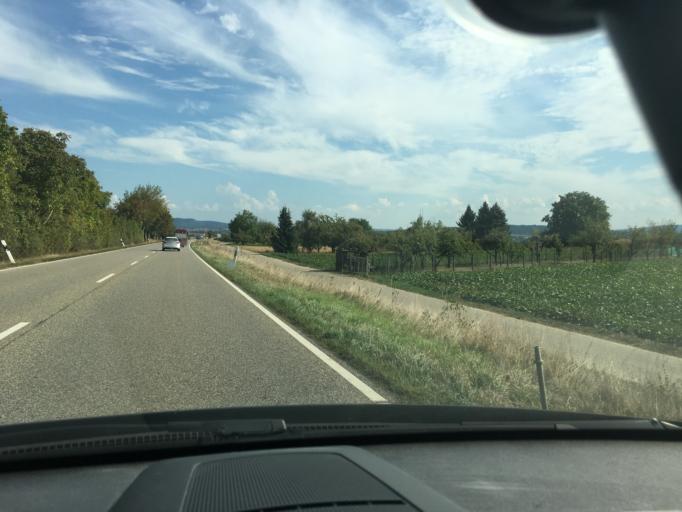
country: DE
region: Baden-Wuerttemberg
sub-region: Regierungsbezirk Stuttgart
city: Stuttgart Muehlhausen
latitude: 48.8861
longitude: 9.2445
